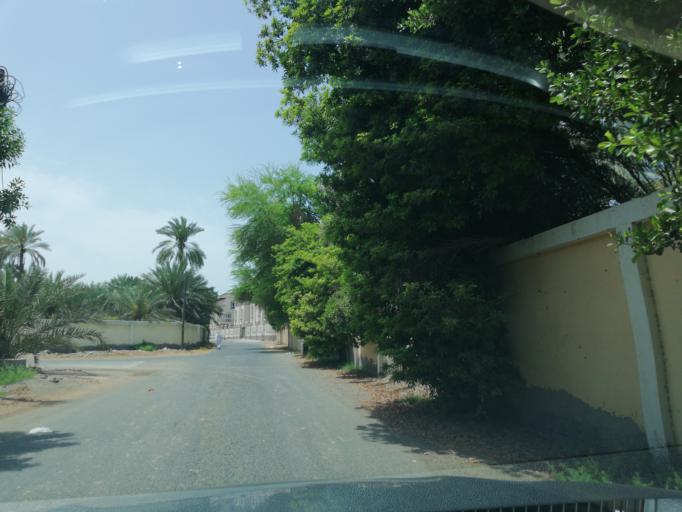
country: OM
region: Muhafazat Masqat
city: As Sib al Jadidah
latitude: 23.6588
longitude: 58.2121
